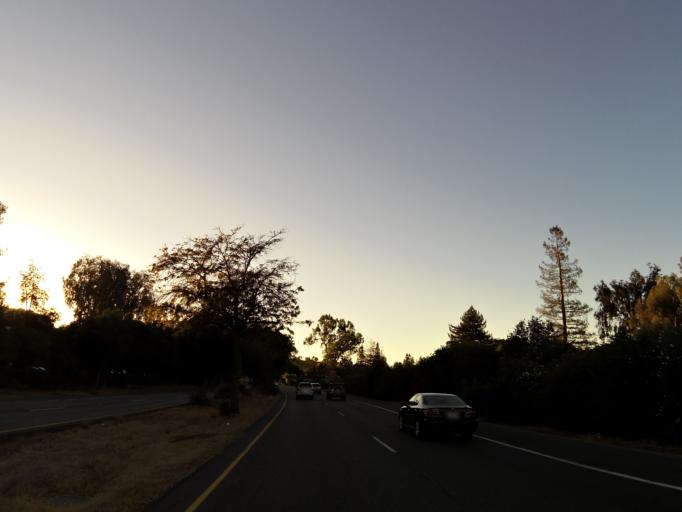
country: US
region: California
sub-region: Santa Clara County
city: Los Altos Hills
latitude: 37.4047
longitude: -122.1472
